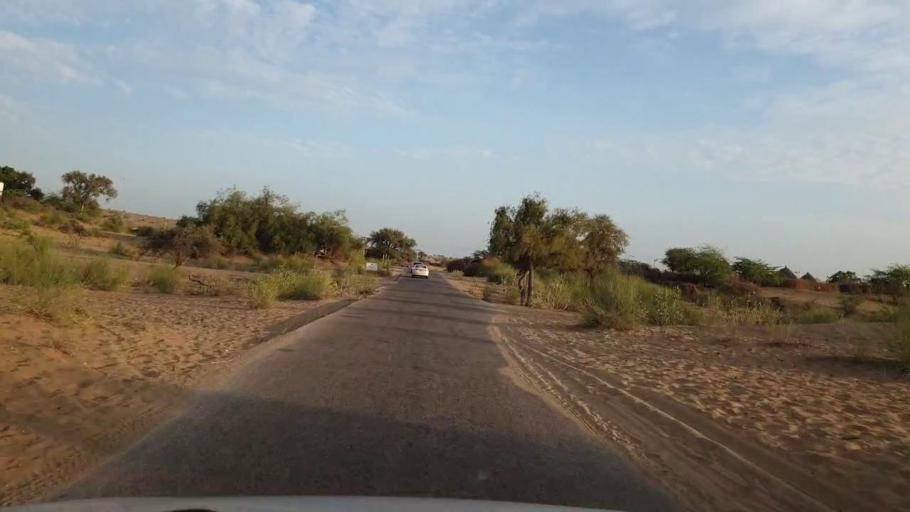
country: PK
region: Sindh
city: Nabisar
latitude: 25.0580
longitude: 69.9655
